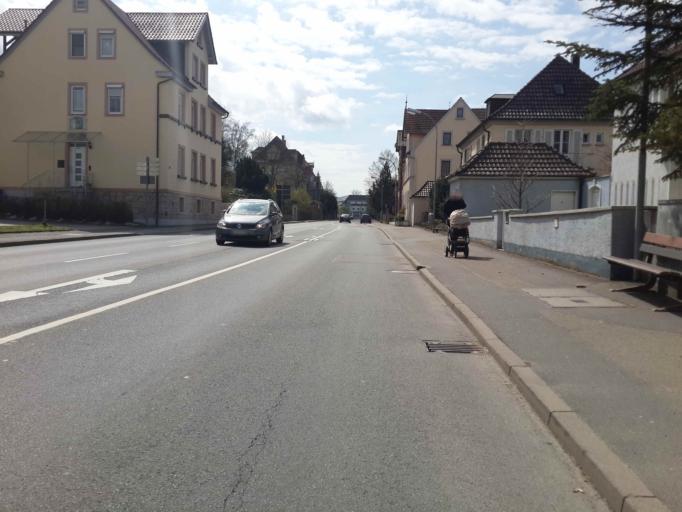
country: DE
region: Baden-Wuerttemberg
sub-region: Regierungsbezirk Stuttgart
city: Bad Mergentheim
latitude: 49.4874
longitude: 9.7723
